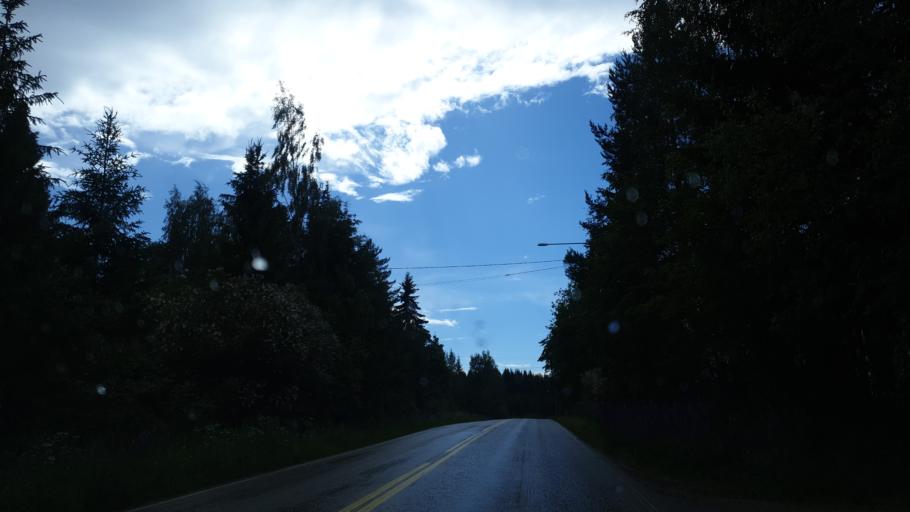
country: FI
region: Northern Savo
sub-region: Kuopio
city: Kuopio
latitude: 62.9082
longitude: 27.8581
